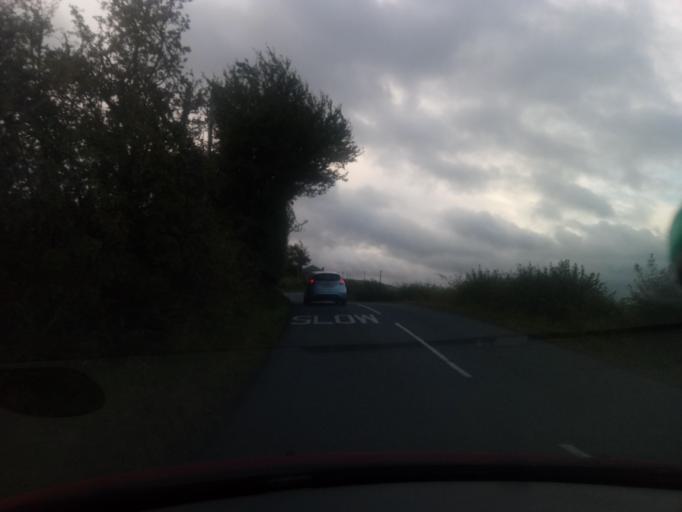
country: GB
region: Scotland
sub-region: The Scottish Borders
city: Jedburgh
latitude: 55.3966
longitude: -2.6503
